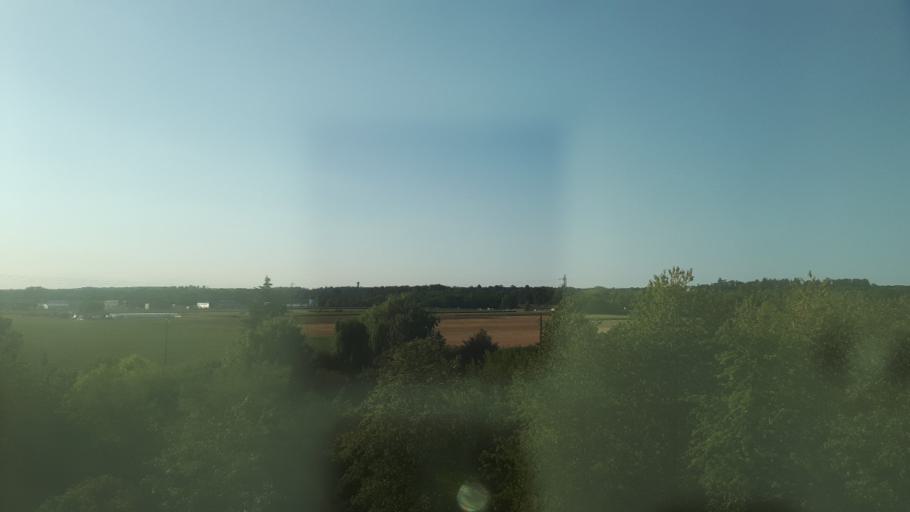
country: FR
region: Centre
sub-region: Departement d'Indre-et-Loire
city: Vouvray
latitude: 47.3955
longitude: 0.7987
